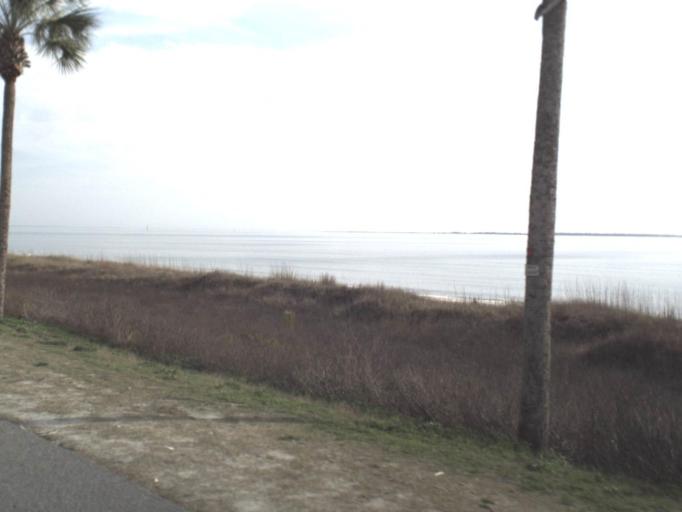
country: US
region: Florida
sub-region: Bay County
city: Mexico Beach
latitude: 29.9313
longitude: -85.3956
